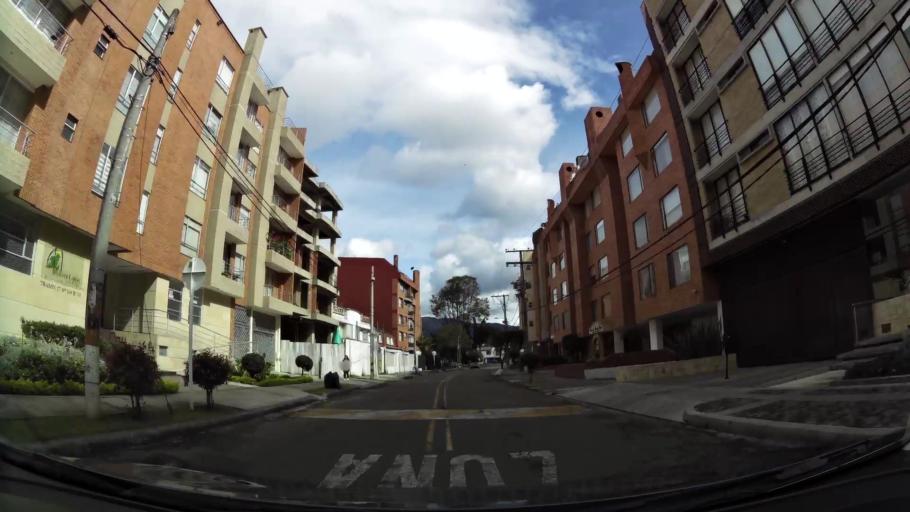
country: CO
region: Bogota D.C.
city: Barrio San Luis
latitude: 4.6938
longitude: -74.0653
